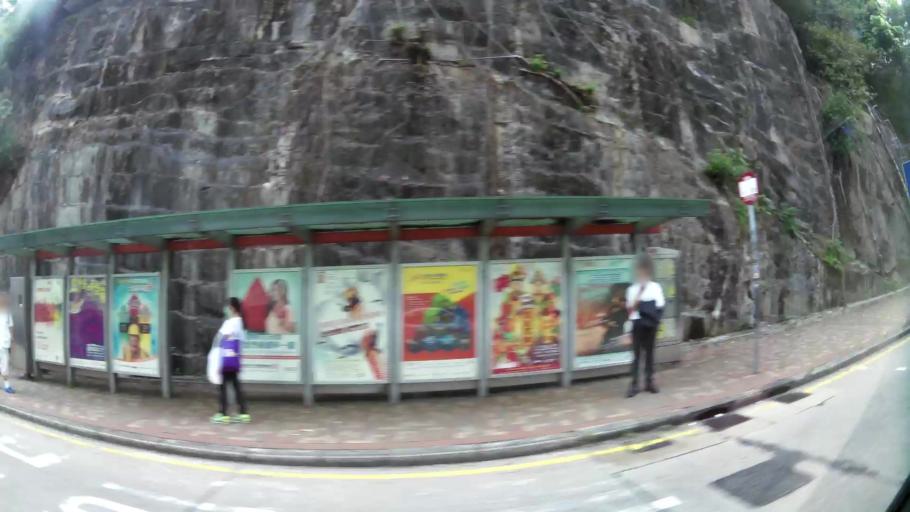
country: HK
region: Kowloon City
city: Kowloon
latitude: 22.3205
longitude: 114.1763
